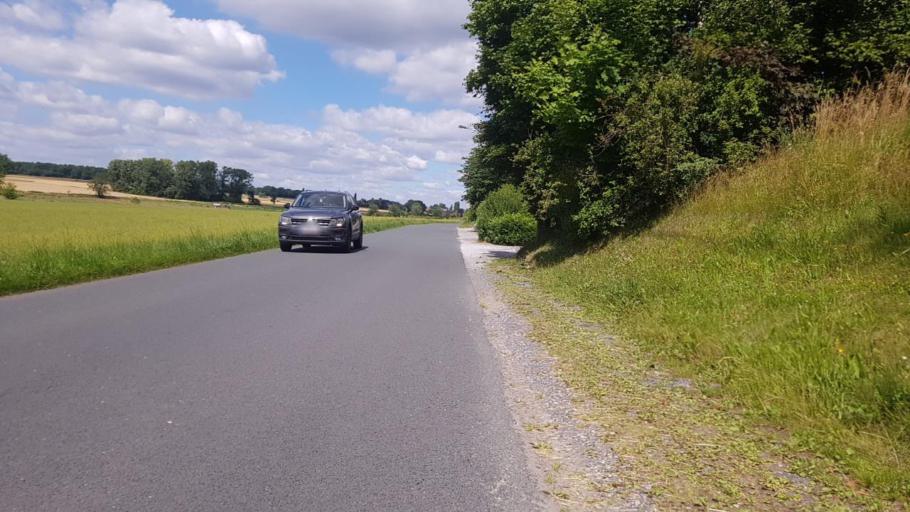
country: BE
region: Wallonia
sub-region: Province de Namur
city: Walcourt
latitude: 50.3295
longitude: 4.3821
